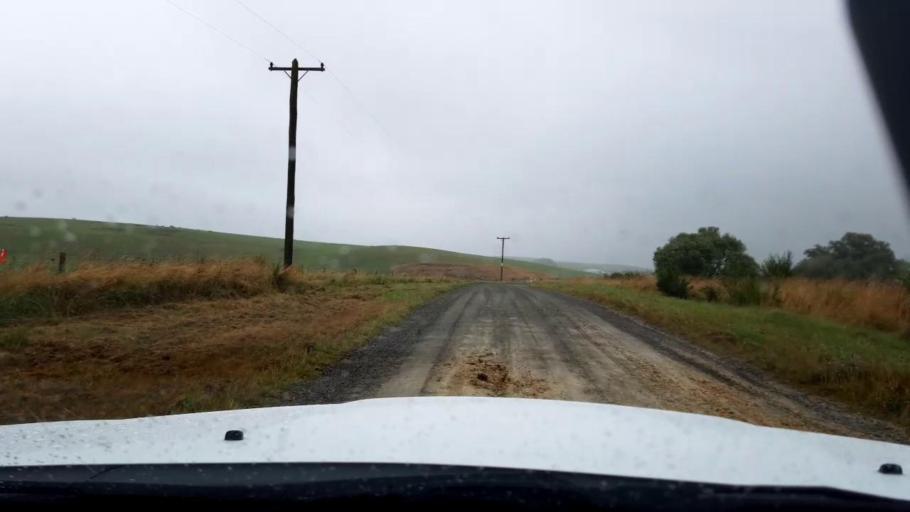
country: NZ
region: Canterbury
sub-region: Timaru District
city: Pleasant Point
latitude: -44.1663
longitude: 171.1926
